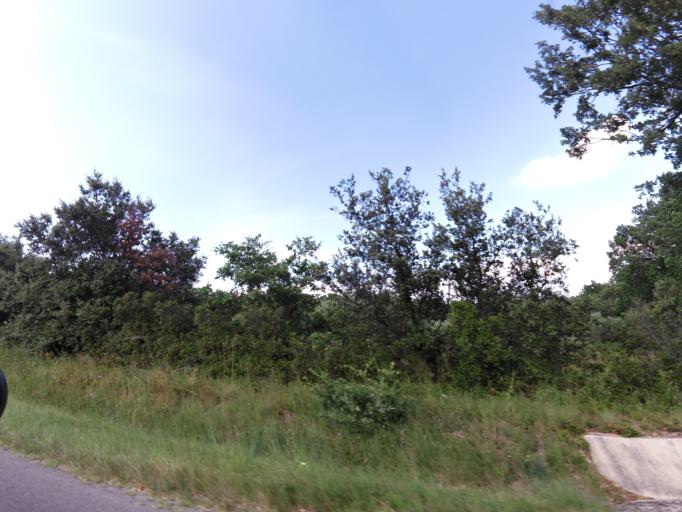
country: FR
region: Languedoc-Roussillon
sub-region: Departement du Gard
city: Sommieres
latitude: 43.8161
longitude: 4.0582
